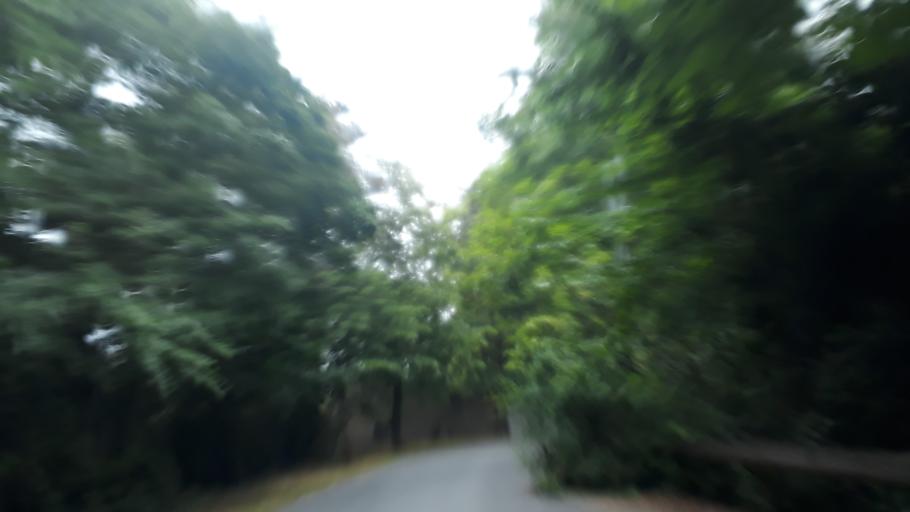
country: FR
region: Ile-de-France
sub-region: Departement de l'Essonne
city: La Ville-du-Bois
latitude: 48.6675
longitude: 2.2745
